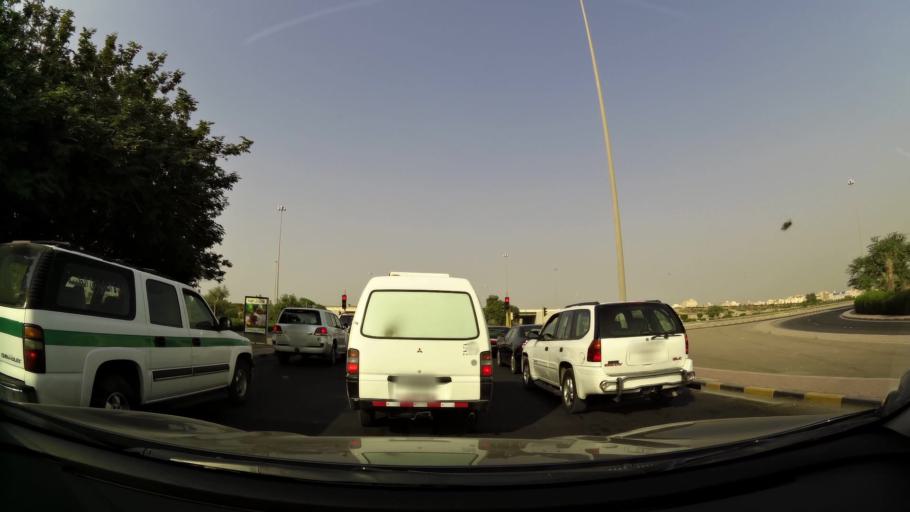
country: KW
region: Mubarak al Kabir
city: Mubarak al Kabir
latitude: 29.1803
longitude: 48.0931
